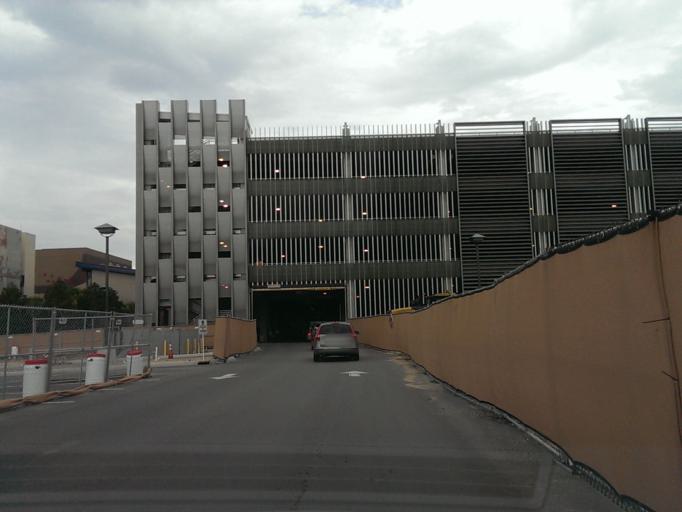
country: US
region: Florida
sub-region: Osceola County
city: Celebration
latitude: 28.3697
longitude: -81.5225
